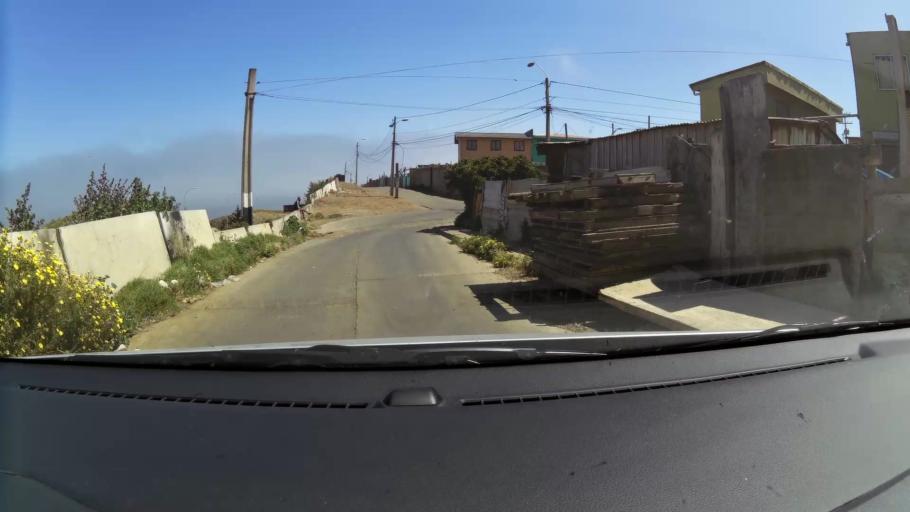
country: CL
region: Valparaiso
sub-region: Provincia de Valparaiso
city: Valparaiso
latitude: -33.0343
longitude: -71.6547
